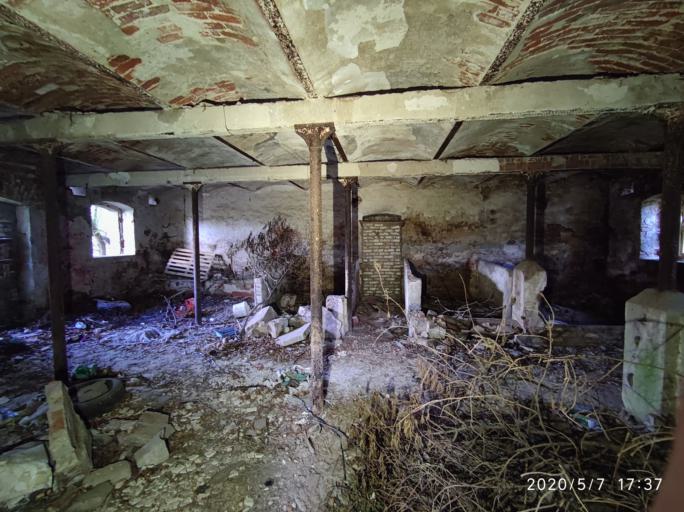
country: PL
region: Lubusz
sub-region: Powiat zielonogorski
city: Sulechow
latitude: 51.9988
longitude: 15.6104
